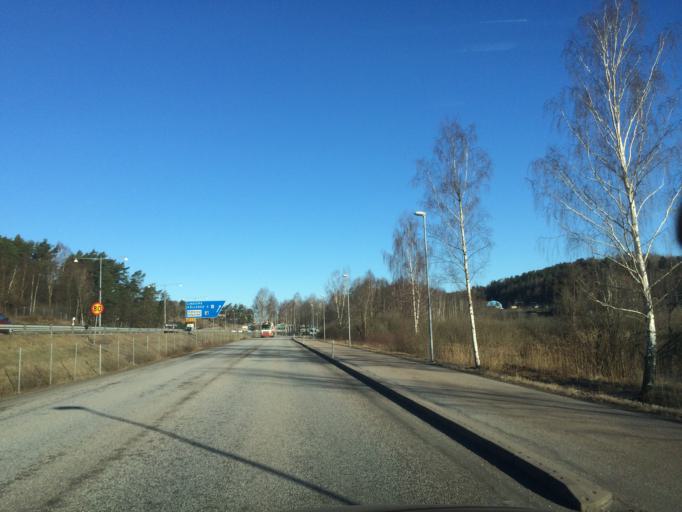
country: SE
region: Vaestra Goetaland
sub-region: Molndal
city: Kallered
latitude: 57.5944
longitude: 12.0609
